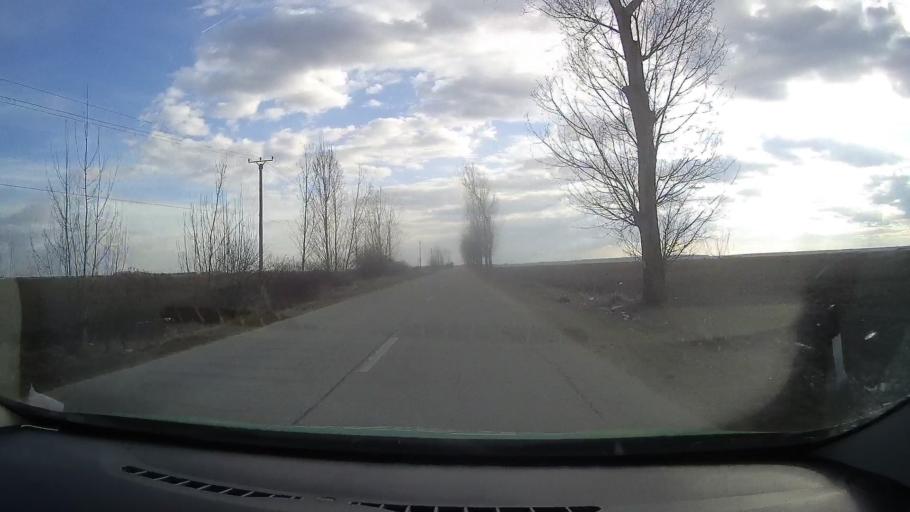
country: RO
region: Dambovita
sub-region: Comuna Vacaresti
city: Vacaresti
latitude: 44.8792
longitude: 25.4636
